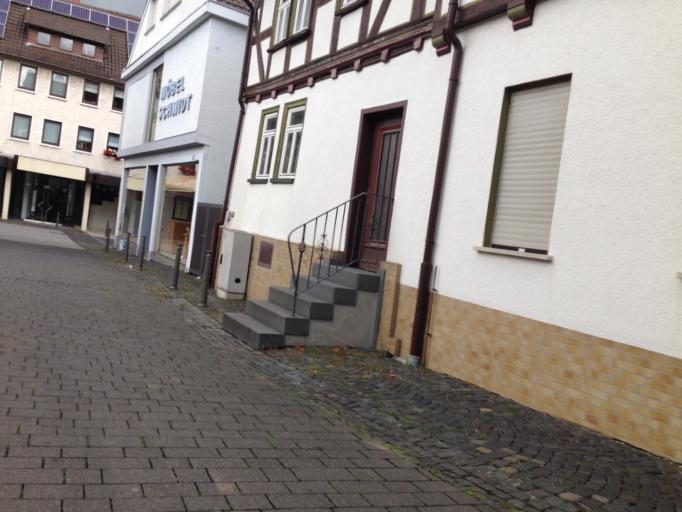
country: DE
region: Hesse
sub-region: Regierungsbezirk Giessen
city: Hungen
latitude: 50.4751
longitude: 8.9011
